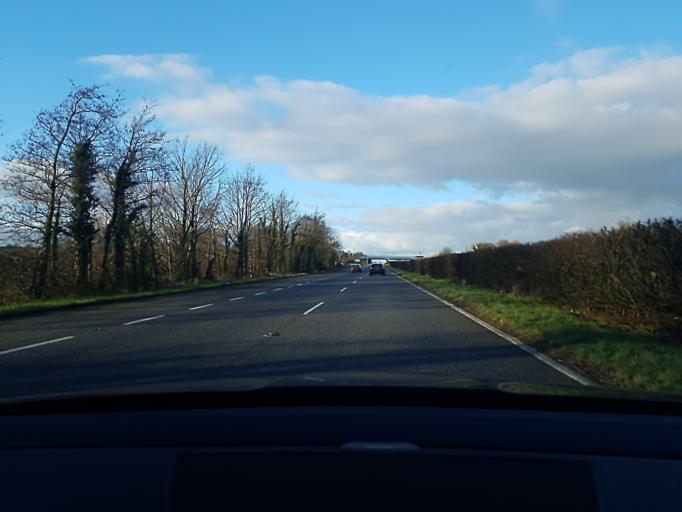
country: IE
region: Munster
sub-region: An Clar
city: Shannon
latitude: 52.7057
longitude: -8.8346
